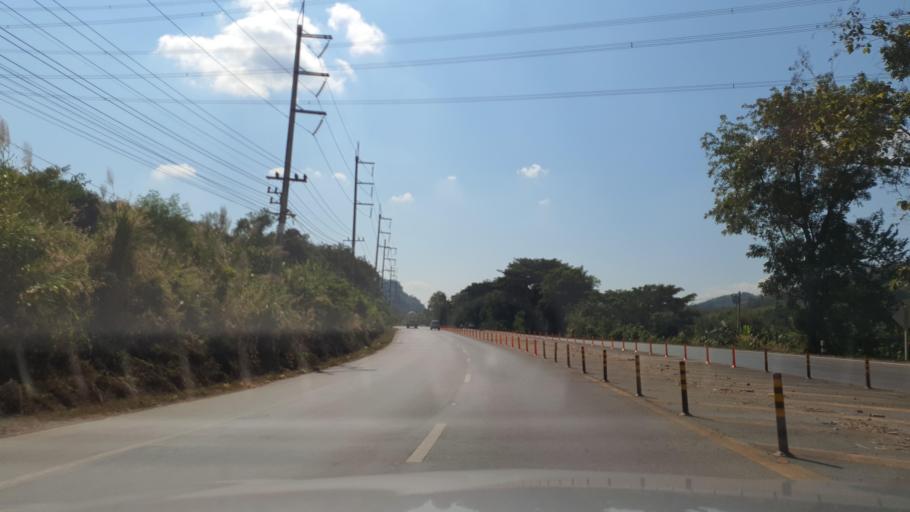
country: TH
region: Nan
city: Nan
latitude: 18.8999
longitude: 100.7568
